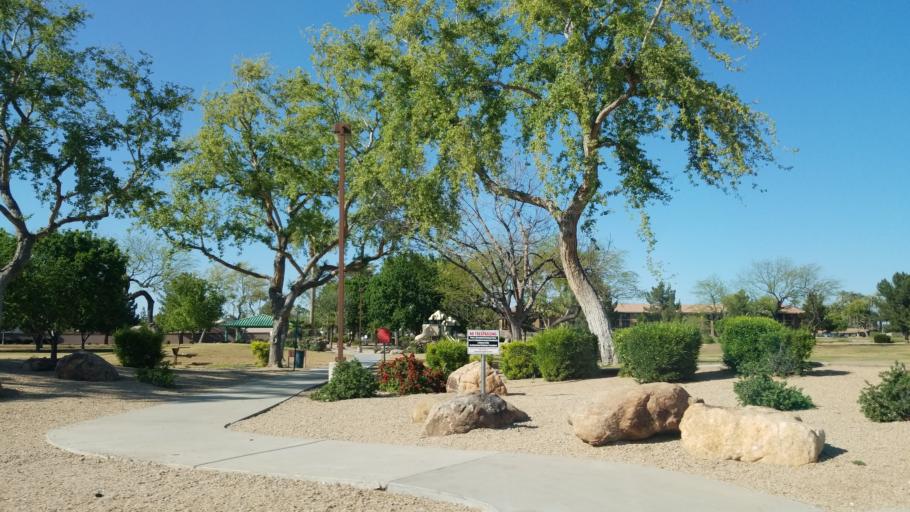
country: US
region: Arizona
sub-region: Maricopa County
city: Glendale
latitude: 33.5496
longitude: -112.1732
